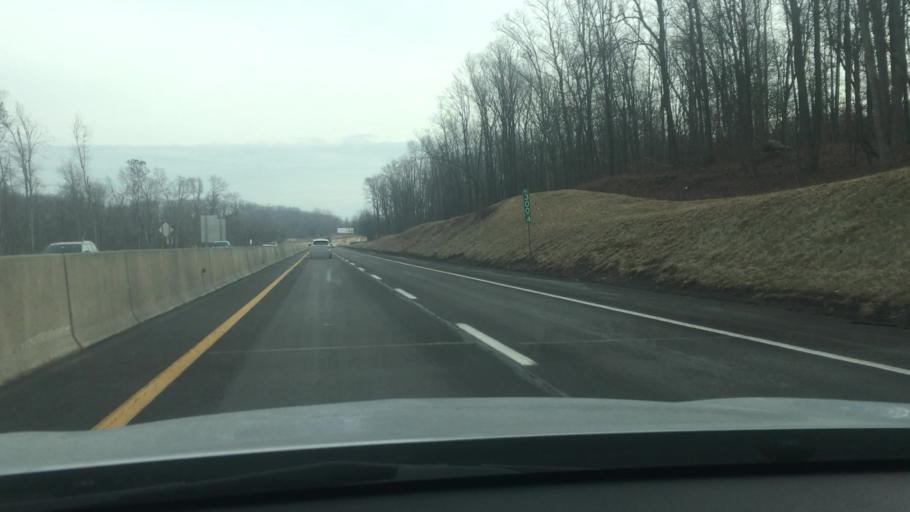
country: US
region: Pennsylvania
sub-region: Chester County
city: Elverson
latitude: 40.1487
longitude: -75.8485
